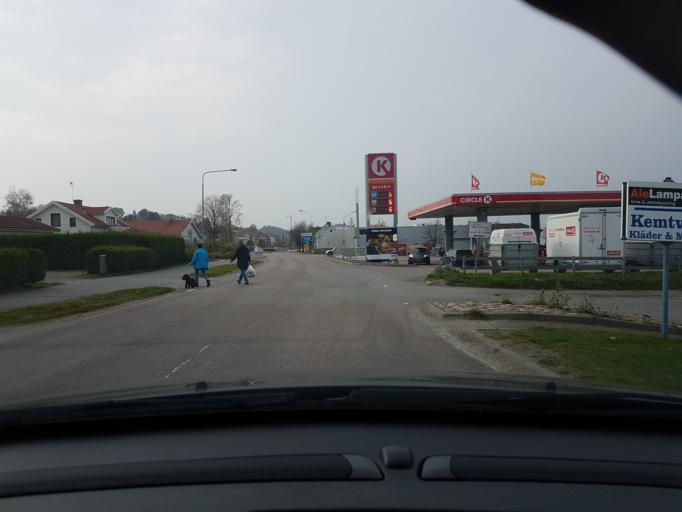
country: SE
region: Vaestra Goetaland
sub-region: Ale Kommun
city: Alvangen
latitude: 57.9601
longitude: 12.1267
